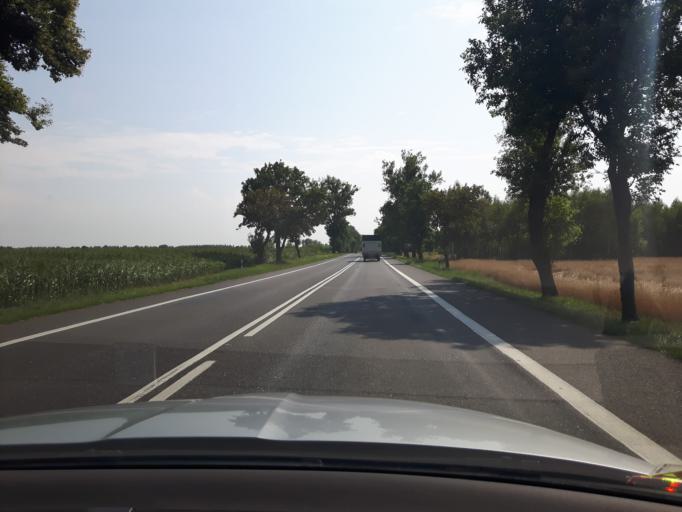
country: PL
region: Masovian Voivodeship
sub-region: Powiat mlawski
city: Wisniewo
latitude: 53.0167
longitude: 20.3333
